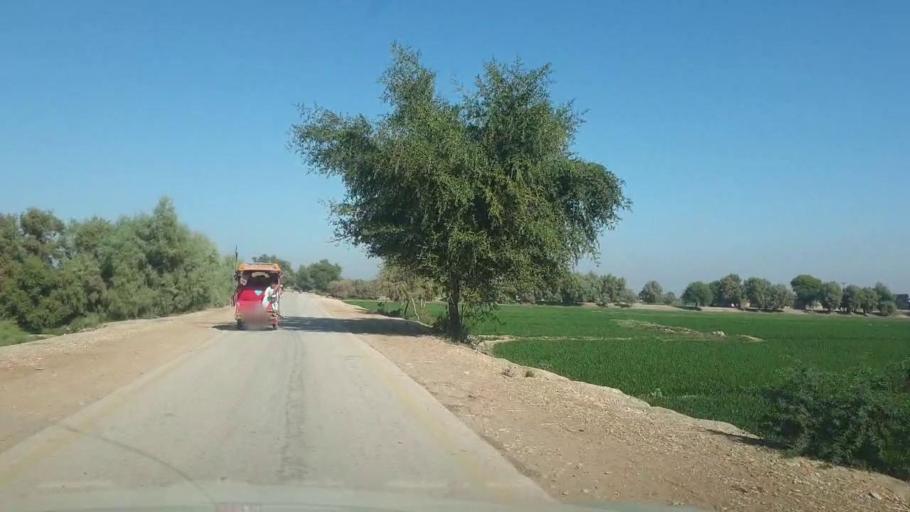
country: PK
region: Sindh
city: Bhan
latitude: 26.5488
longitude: 67.6337
